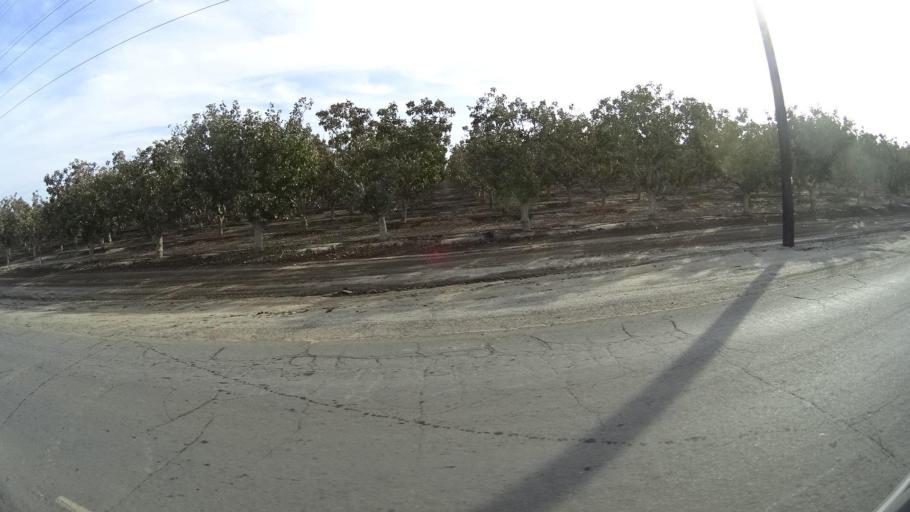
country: US
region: California
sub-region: Kern County
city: McFarland
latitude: 35.7209
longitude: -119.2051
